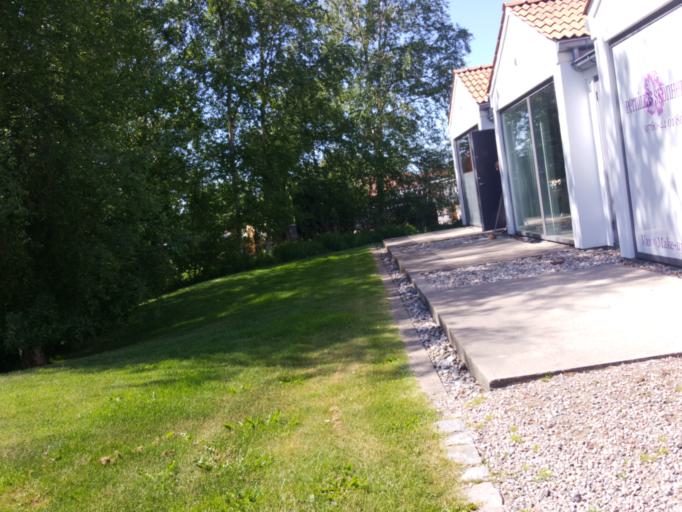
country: SE
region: Halland
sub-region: Laholms Kommun
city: Mellbystrand
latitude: 56.5125
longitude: 12.9488
